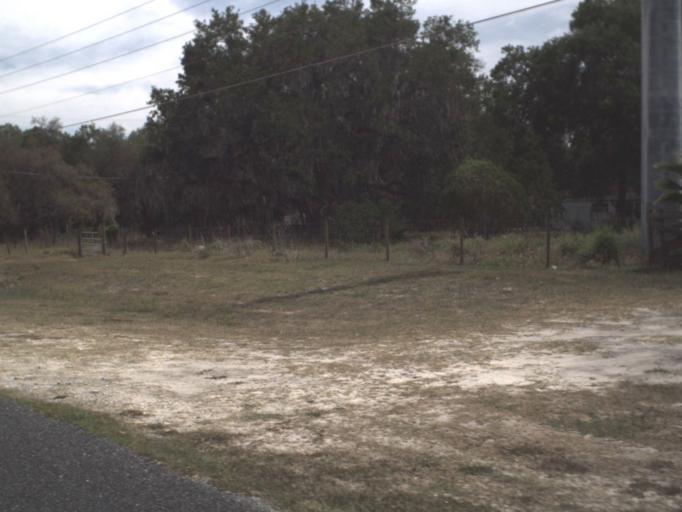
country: US
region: Florida
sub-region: Lake County
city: Fruitland Park
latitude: 28.8228
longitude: -81.9661
